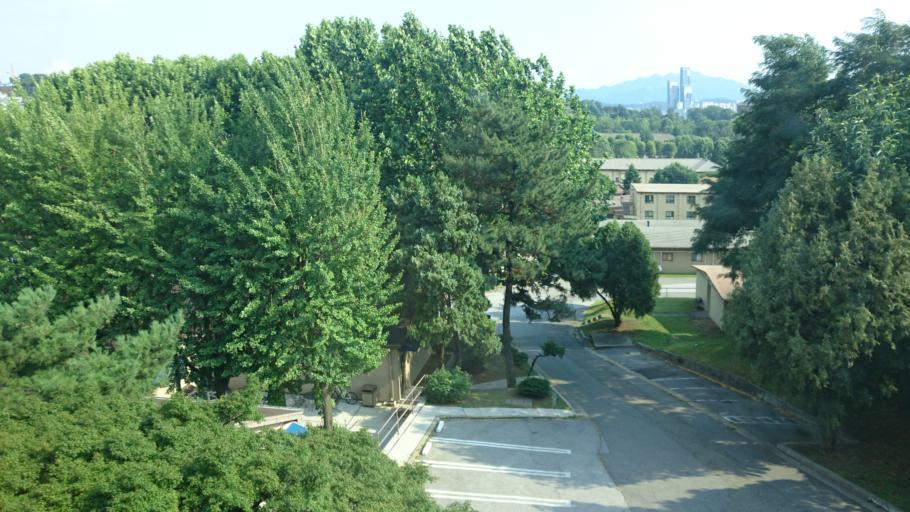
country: KR
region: Seoul
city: Seoul
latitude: 37.5406
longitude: 126.9846
